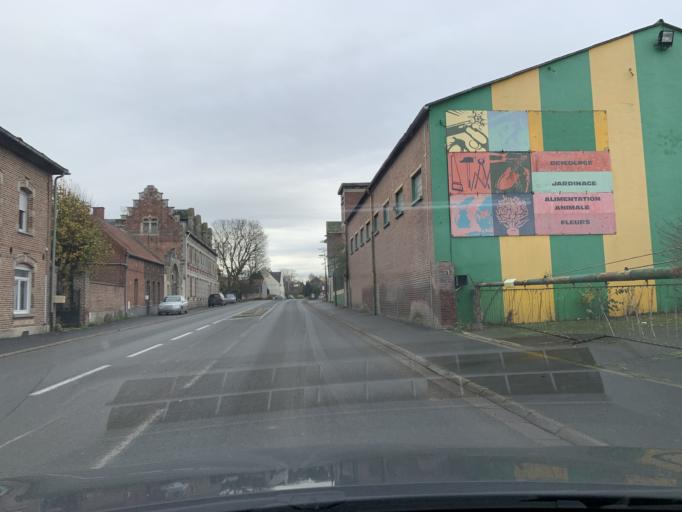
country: FR
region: Nord-Pas-de-Calais
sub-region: Departement du Nord
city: Aubigny-au-Bac
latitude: 50.2563
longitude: 3.1602
